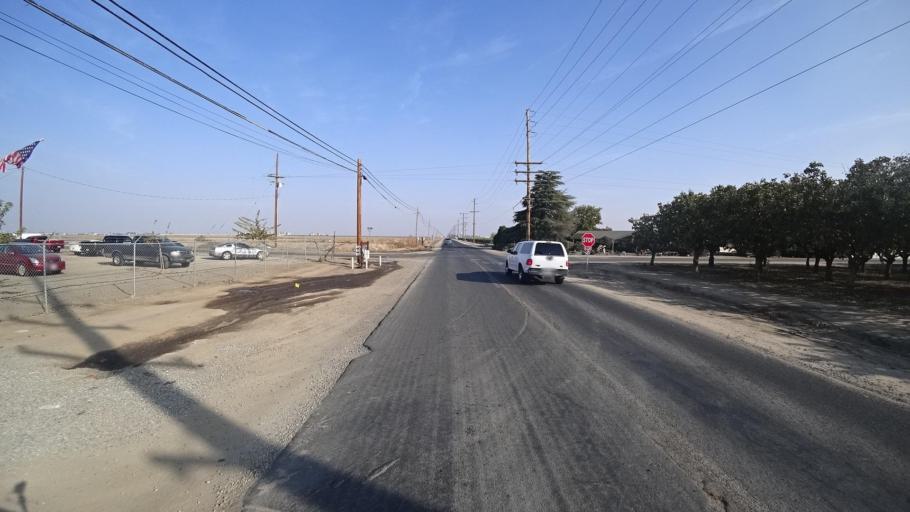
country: US
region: California
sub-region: Kern County
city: Delano
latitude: 35.7758
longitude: -119.2058
